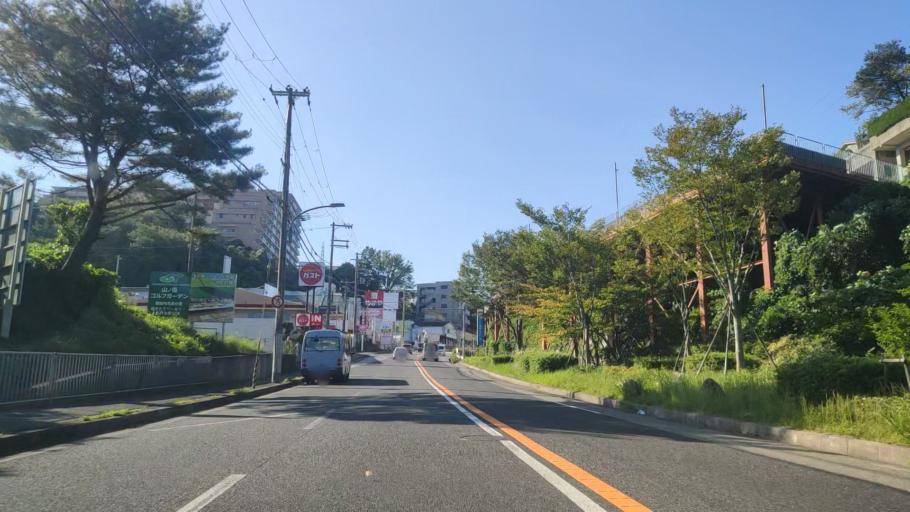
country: JP
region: Hyogo
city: Kobe
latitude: 34.7414
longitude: 135.1591
